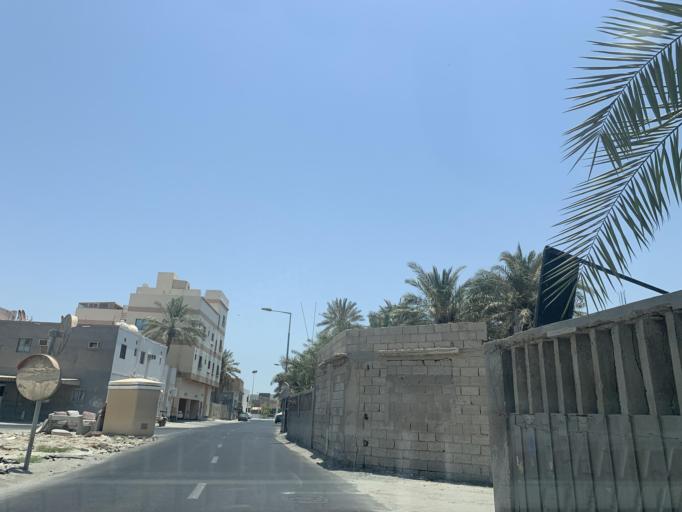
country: BH
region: Muharraq
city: Al Muharraq
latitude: 26.2837
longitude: 50.6200
